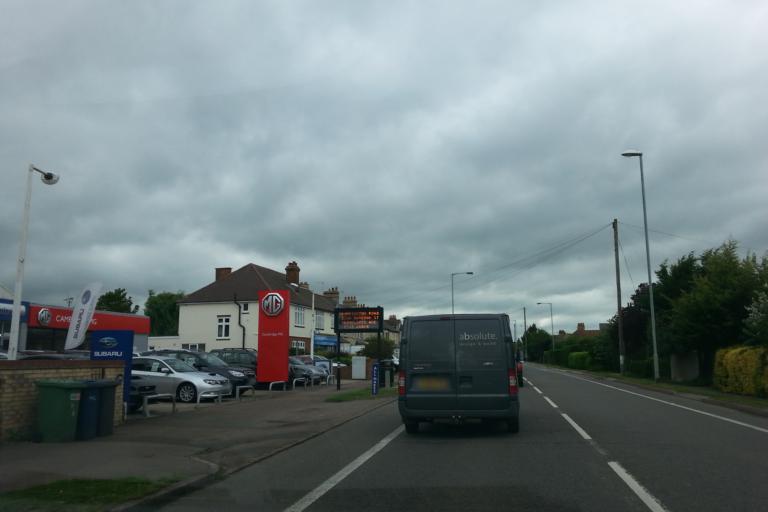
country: GB
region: England
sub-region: Cambridgeshire
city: Grantchester
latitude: 52.1657
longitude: 0.1199
